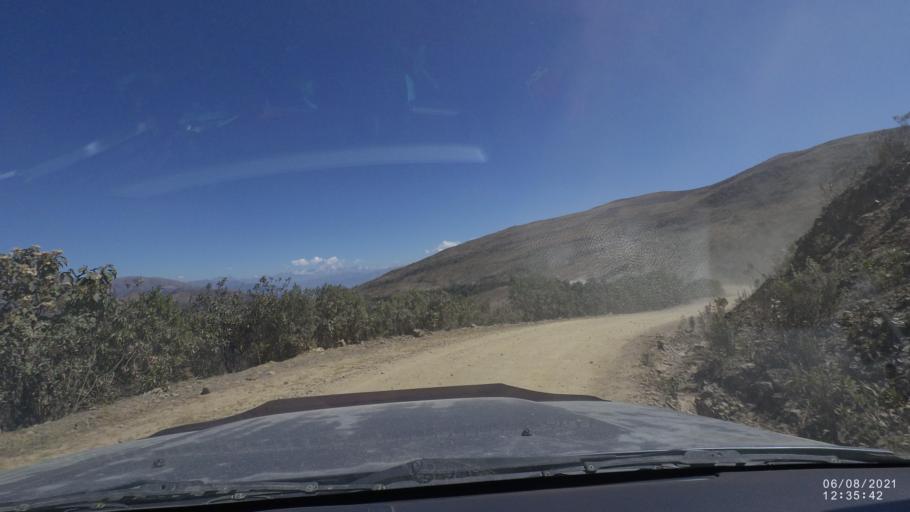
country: BO
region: Cochabamba
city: Colchani
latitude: -16.7783
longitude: -66.6499
